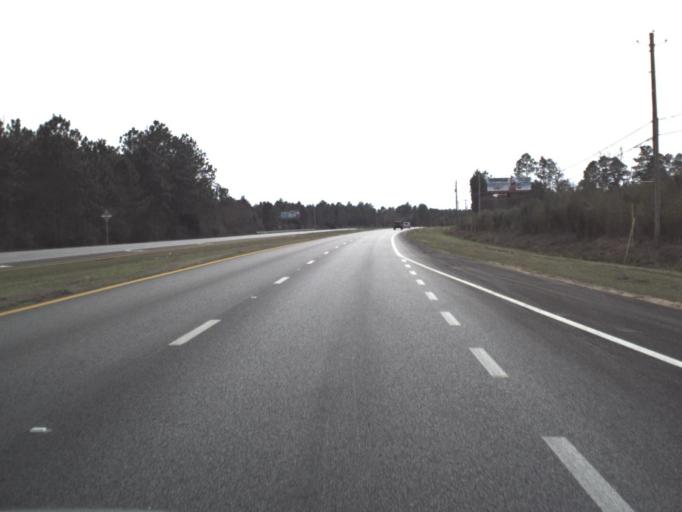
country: US
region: Florida
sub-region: Bay County
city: Youngstown
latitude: 30.3341
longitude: -85.4438
